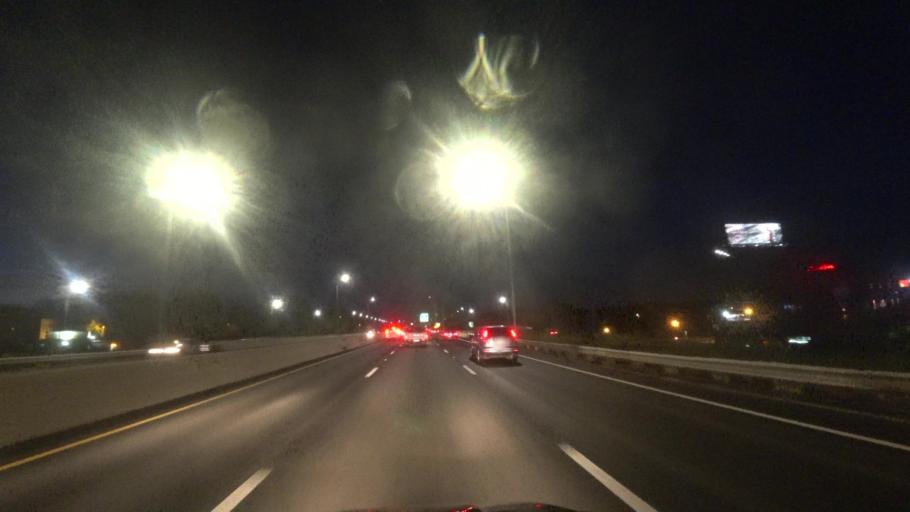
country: US
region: Massachusetts
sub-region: Essex County
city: North Andover
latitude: 42.7050
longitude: -71.1394
